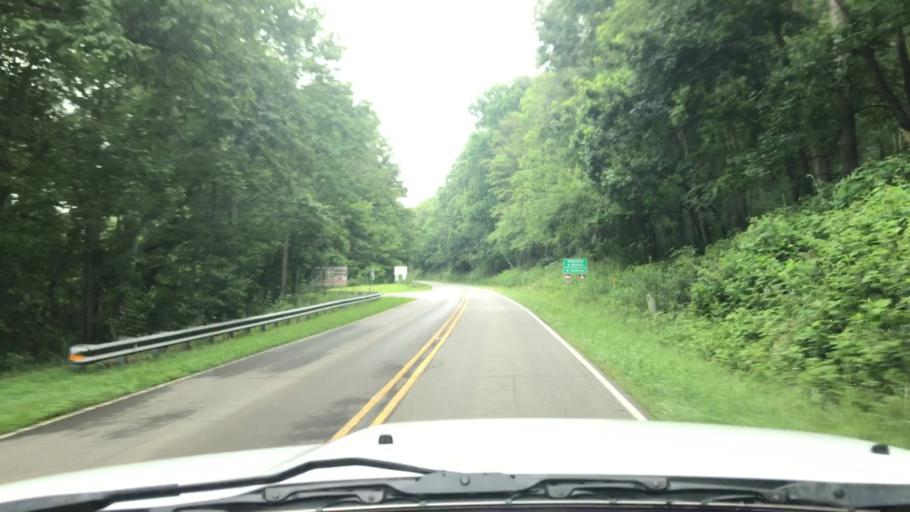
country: US
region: North Carolina
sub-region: Graham County
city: Robbinsville
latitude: 35.3691
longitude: -83.8514
